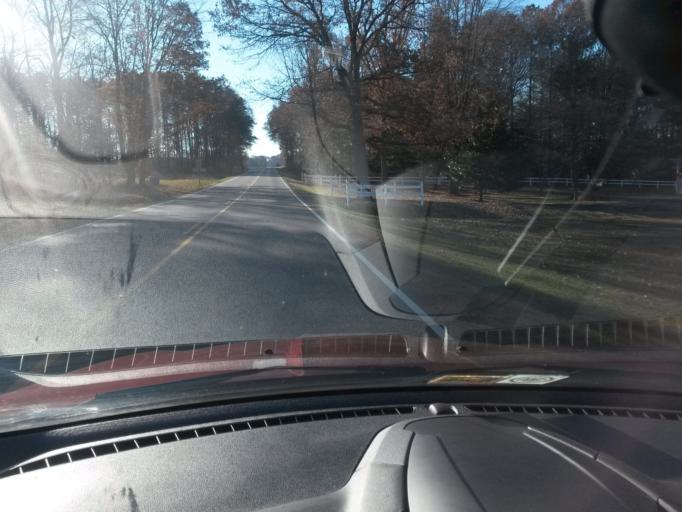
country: US
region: Virginia
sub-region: Charlotte County
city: Charlotte Court House
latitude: 37.1628
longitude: -78.7032
